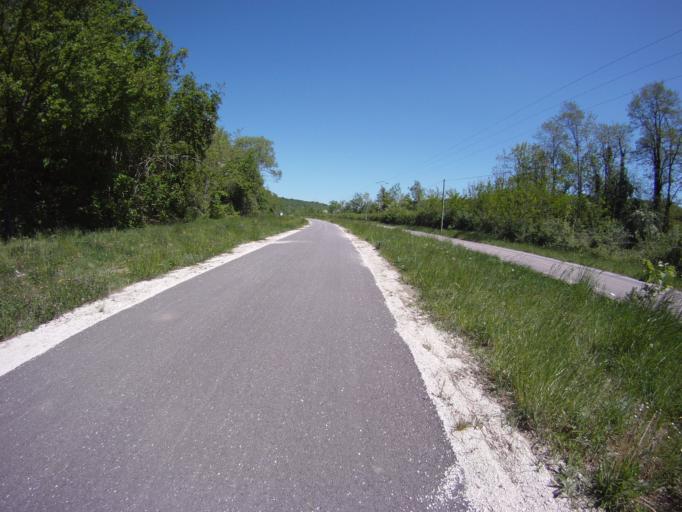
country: FR
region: Lorraine
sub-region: Departement de Meurthe-et-Moselle
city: Villey-Saint-Etienne
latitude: 48.7450
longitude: 6.0034
